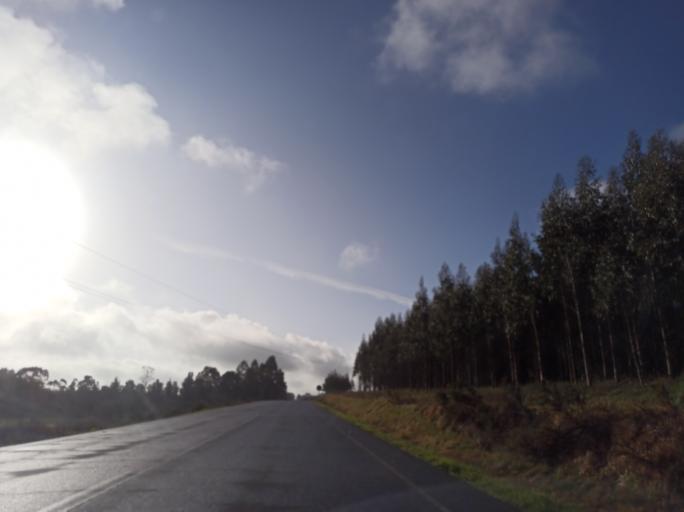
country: ES
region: Galicia
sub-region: Provincia da Coruna
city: Curtis
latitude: 43.1209
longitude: -8.0292
